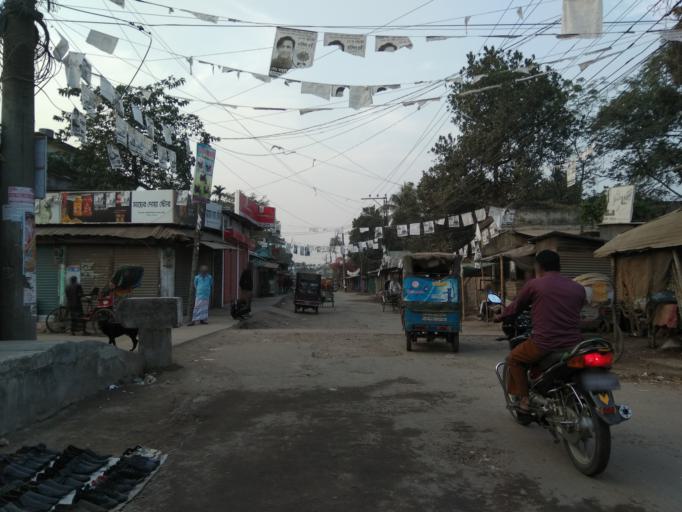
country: BD
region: Rangpur Division
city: Rangpur
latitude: 25.7299
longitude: 89.2633
